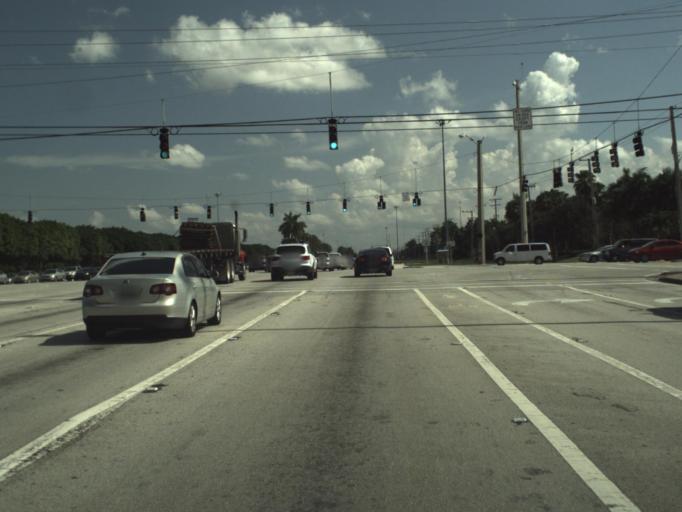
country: US
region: Florida
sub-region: Palm Beach County
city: Wellington
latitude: 26.6513
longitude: -80.2037
